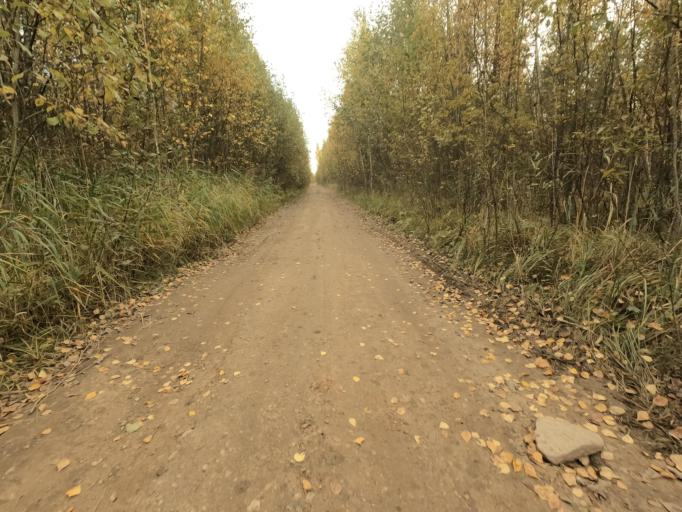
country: RU
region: Novgorod
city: Pankovka
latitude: 58.8769
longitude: 30.8668
